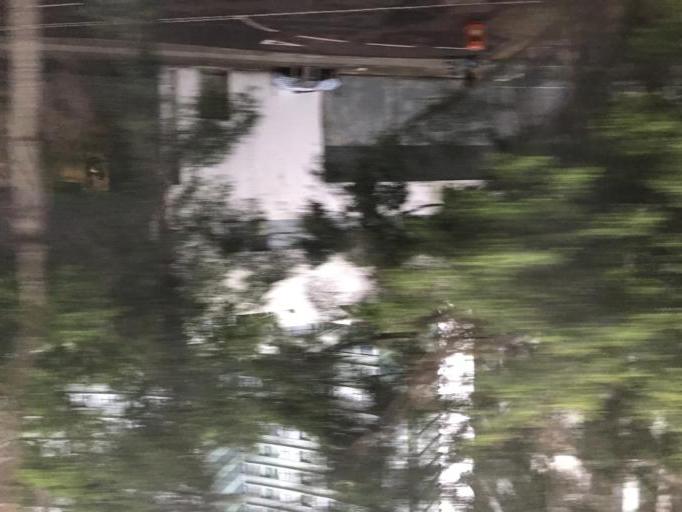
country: HK
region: Sha Tin
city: Sha Tin
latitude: 22.4117
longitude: 114.2105
